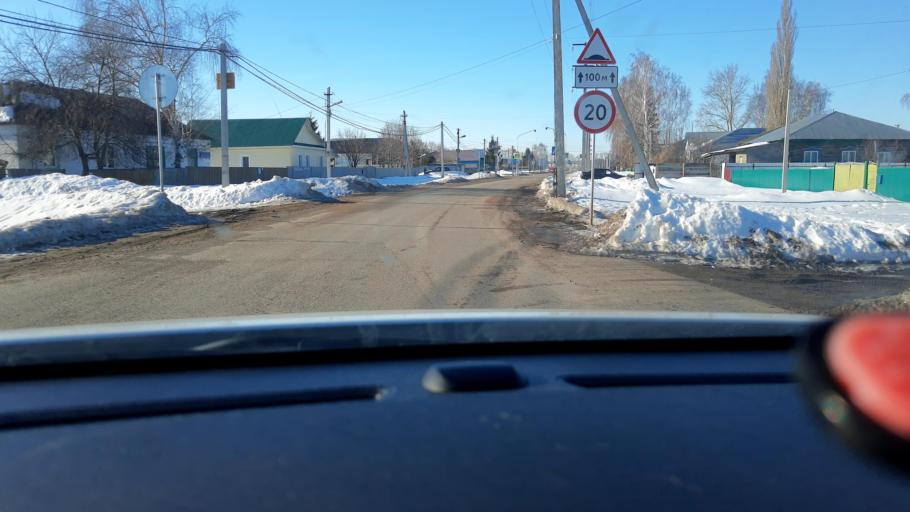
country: RU
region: Bashkortostan
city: Kabakovo
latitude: 54.5186
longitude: 55.9471
